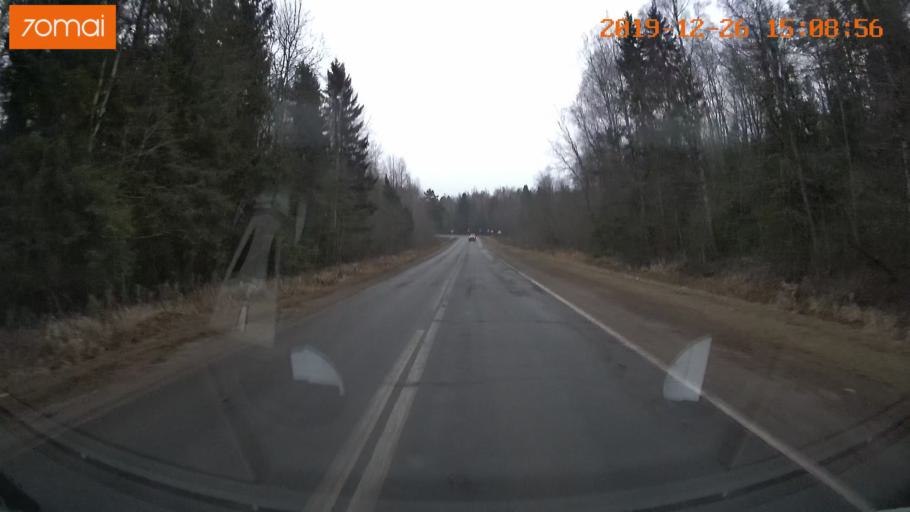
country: RU
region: Jaroslavl
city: Rybinsk
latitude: 58.1541
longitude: 38.8375
